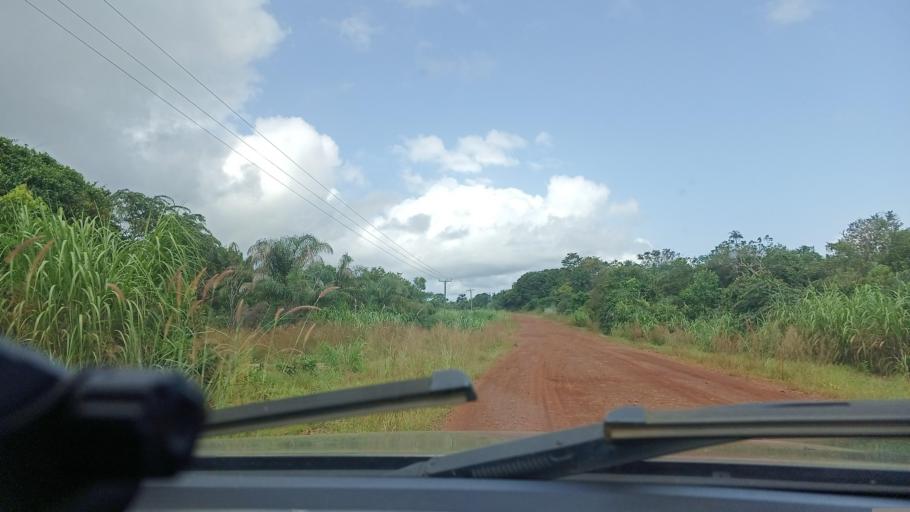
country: LR
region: Grand Cape Mount
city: Robertsport
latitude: 6.6907
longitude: -11.2622
